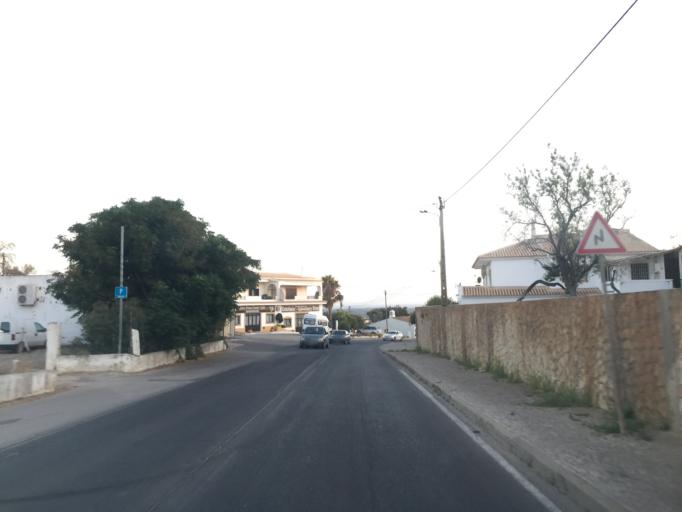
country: PT
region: Faro
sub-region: Loule
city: Almancil
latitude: 37.1020
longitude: -8.0214
